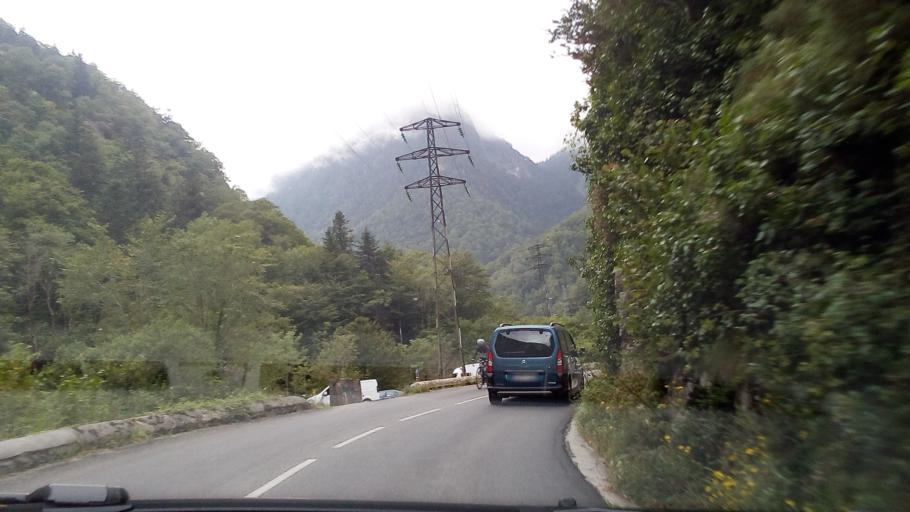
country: FR
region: Aquitaine
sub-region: Departement des Pyrenees-Atlantiques
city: Laruns
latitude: 42.9370
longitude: -0.4437
